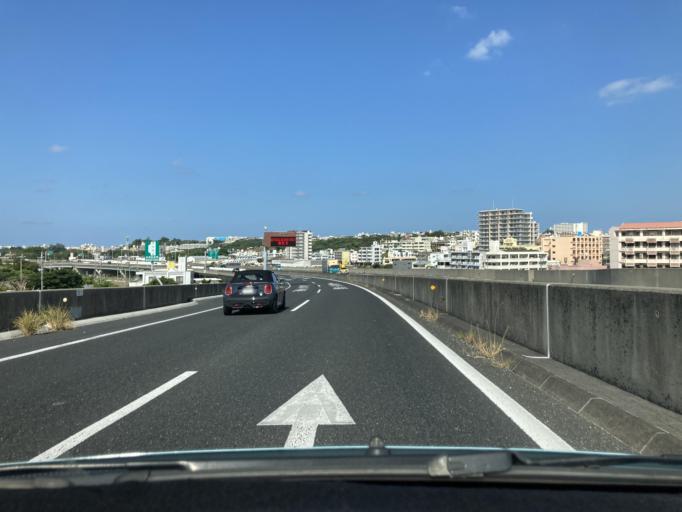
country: JP
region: Okinawa
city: Tomigusuku
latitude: 26.1736
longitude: 127.6757
